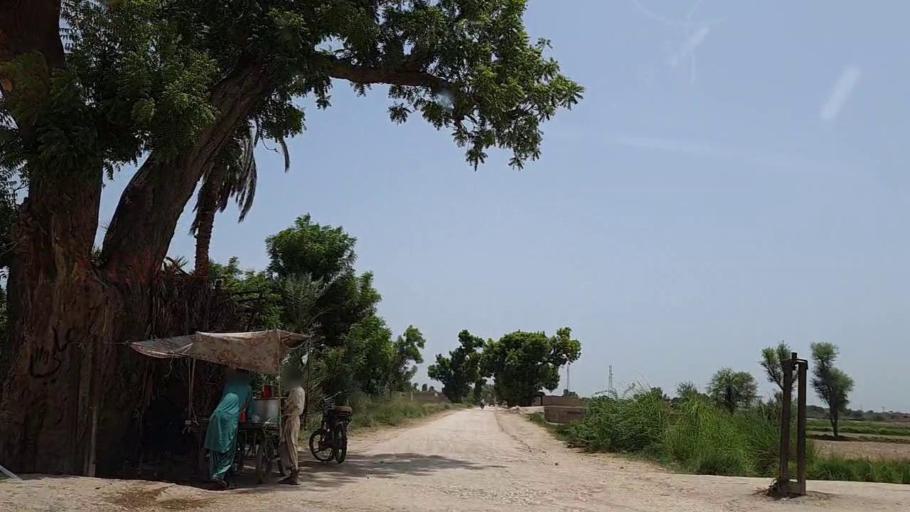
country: PK
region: Sindh
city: Tharu Shah
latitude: 26.9463
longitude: 68.1068
